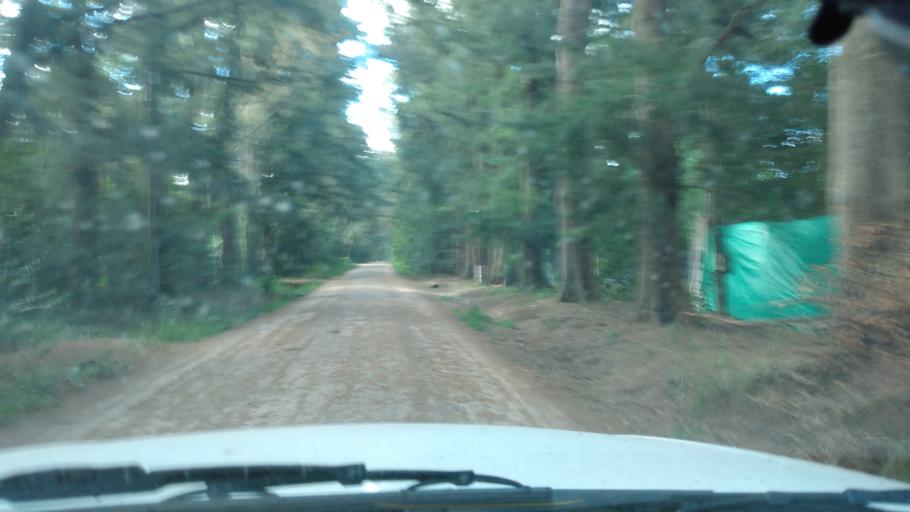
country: AR
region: Buenos Aires
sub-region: Partido de Lujan
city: Lujan
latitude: -34.5540
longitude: -59.1573
